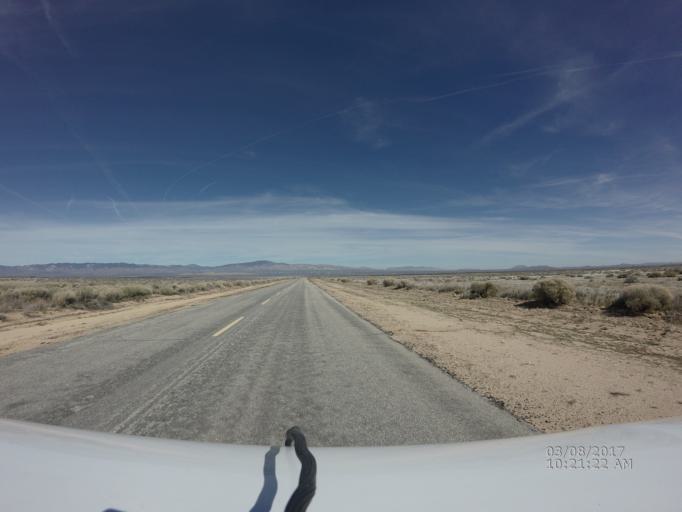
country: US
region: California
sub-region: Los Angeles County
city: Green Valley
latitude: 34.7543
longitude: -118.4312
